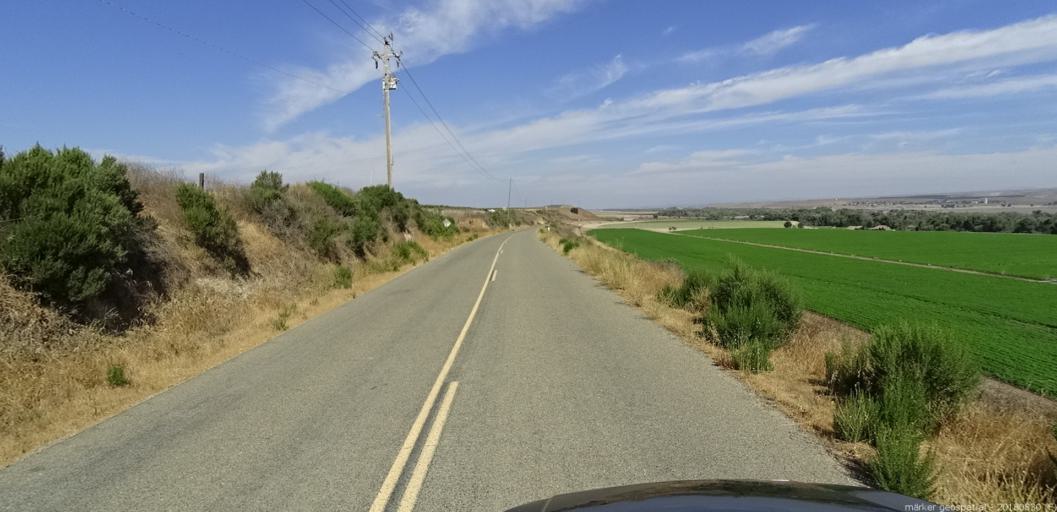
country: US
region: California
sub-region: Monterey County
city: King City
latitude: 36.0967
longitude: -121.0198
